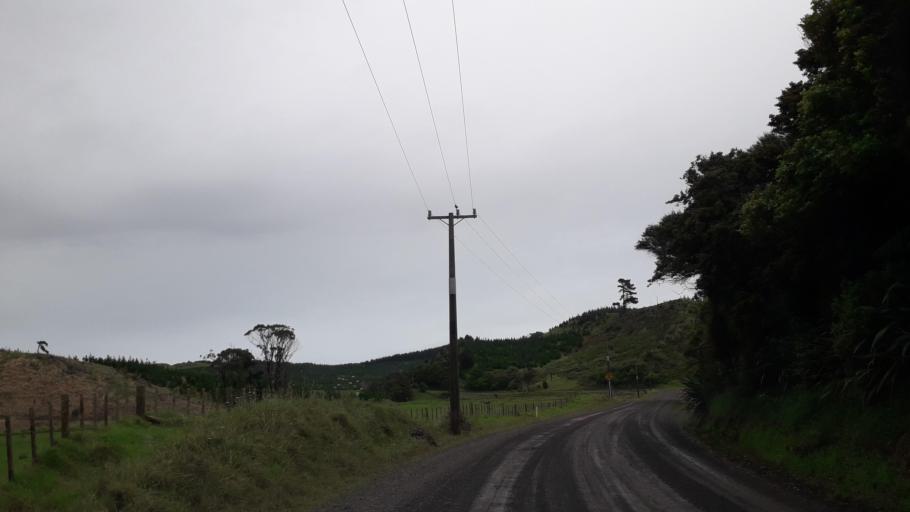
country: NZ
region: Northland
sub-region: Far North District
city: Ahipara
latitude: -35.4303
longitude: 173.3509
